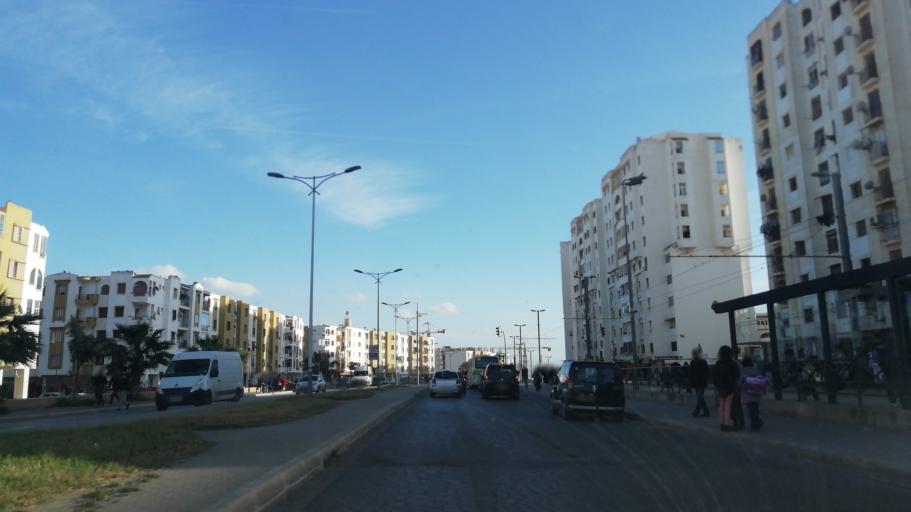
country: DZ
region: Oran
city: Bir el Djir
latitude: 35.7036
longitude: -0.5700
